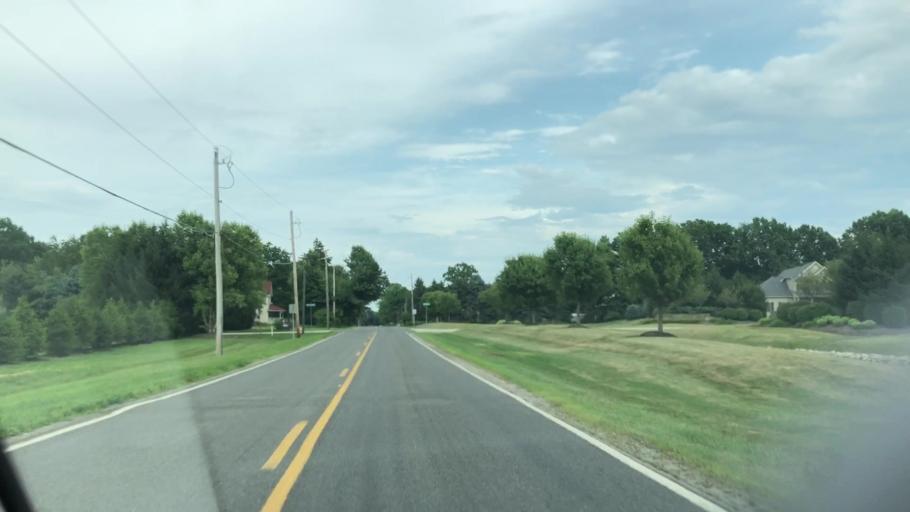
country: US
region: Ohio
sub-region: Summit County
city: Montrose-Ghent
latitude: 41.1178
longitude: -81.7083
